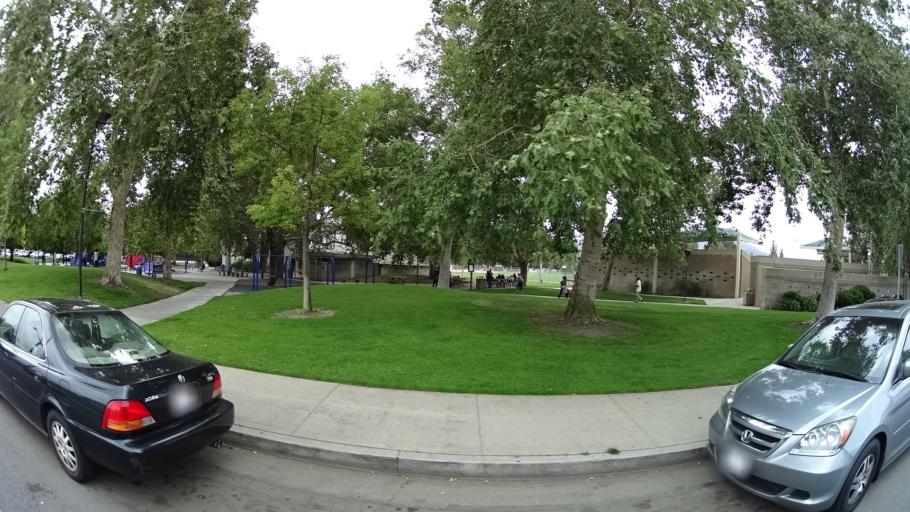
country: US
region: California
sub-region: Los Angeles County
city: Burbank
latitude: 34.1729
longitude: -118.3200
